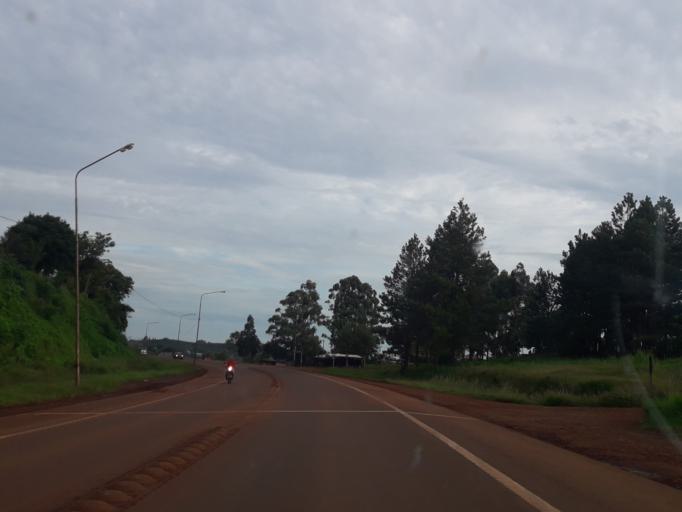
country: AR
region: Misiones
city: Dos de Mayo
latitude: -26.9856
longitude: -54.4764
